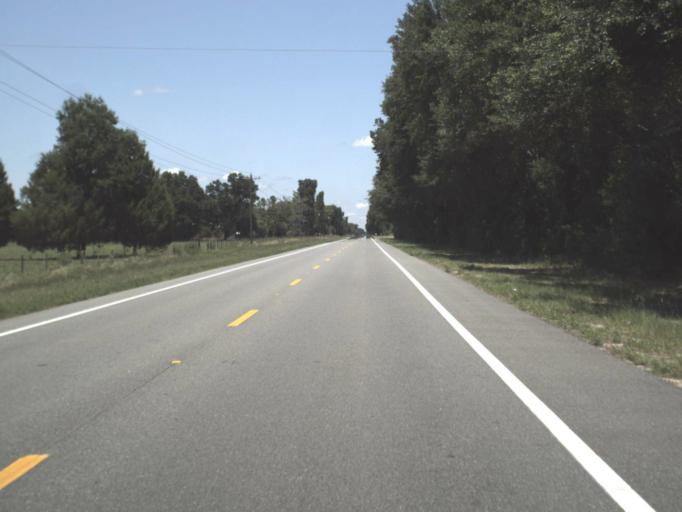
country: US
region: Florida
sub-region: Dixie County
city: Cross City
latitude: 29.7631
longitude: -82.9813
